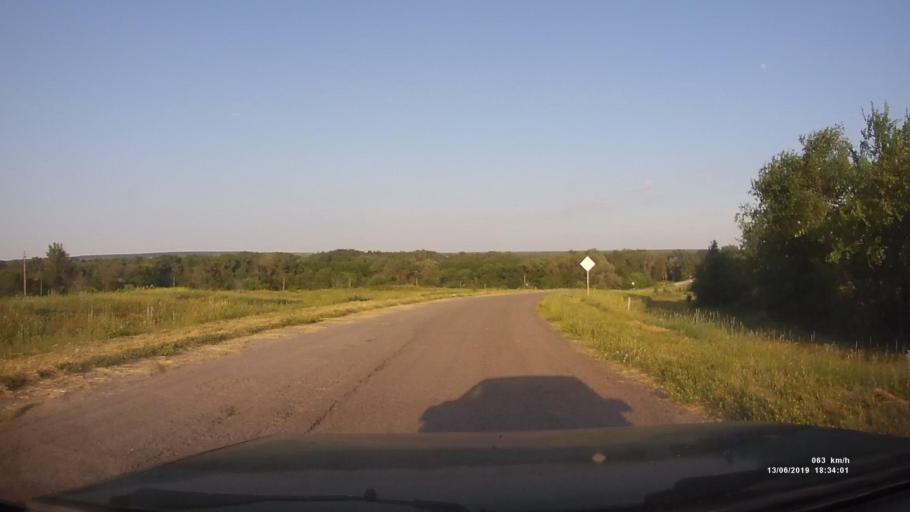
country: RU
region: Rostov
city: Kazanskaya
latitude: 49.8702
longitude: 41.3915
